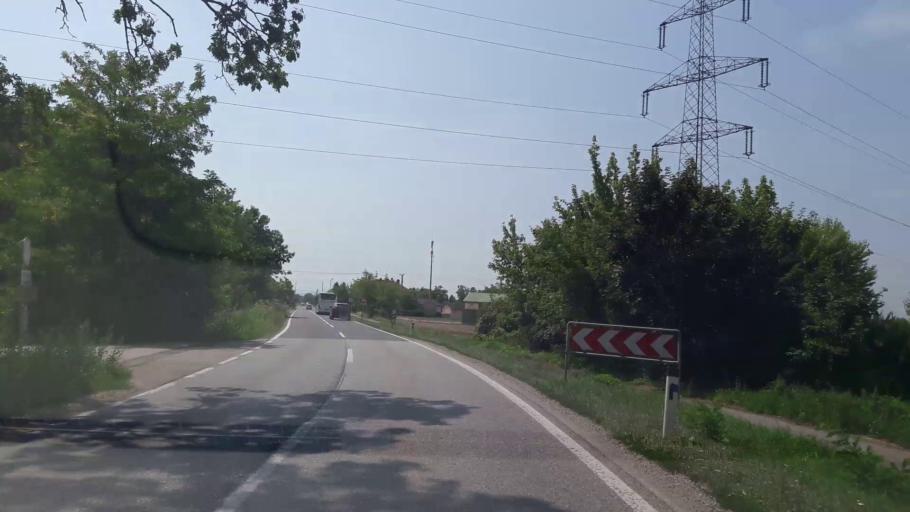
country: AT
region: Lower Austria
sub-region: Politischer Bezirk Bruck an der Leitha
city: Gotzendorf an der Leitha
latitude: 48.0274
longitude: 16.5905
